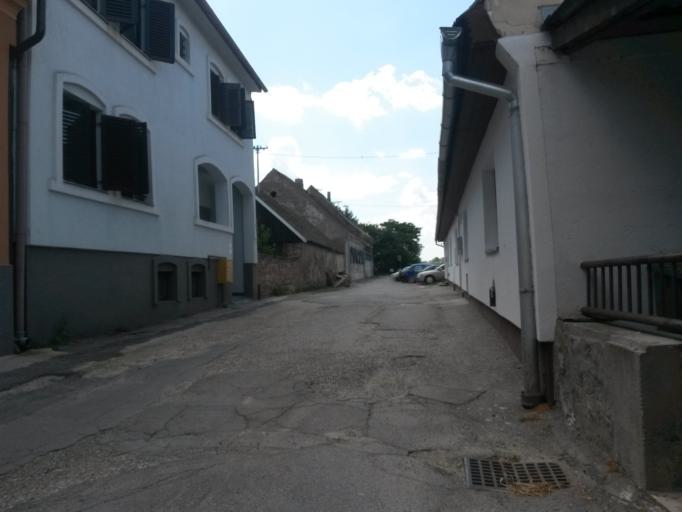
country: HR
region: Osjecko-Baranjska
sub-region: Grad Osijek
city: Osijek
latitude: 45.5605
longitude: 18.7171
